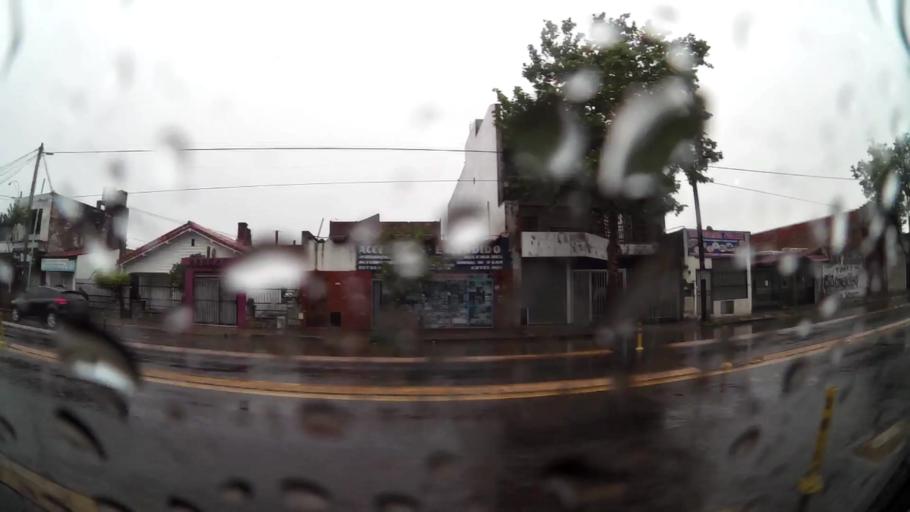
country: AR
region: Buenos Aires F.D.
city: Villa Lugano
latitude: -34.6613
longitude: -58.4450
